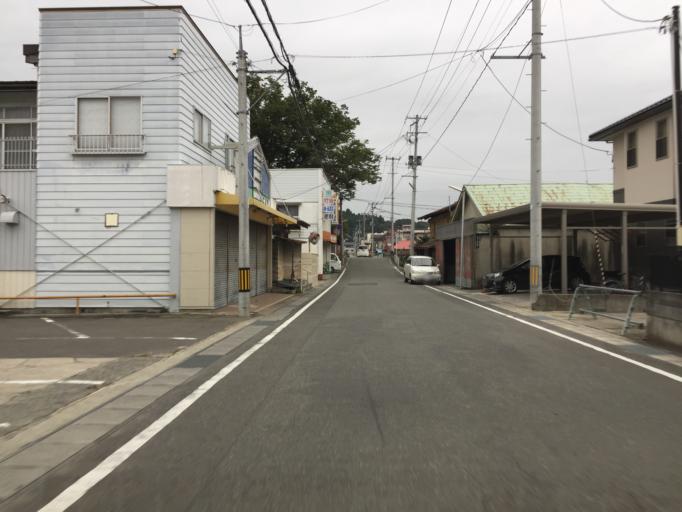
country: JP
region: Fukushima
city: Nihommatsu
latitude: 37.6541
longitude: 140.4586
